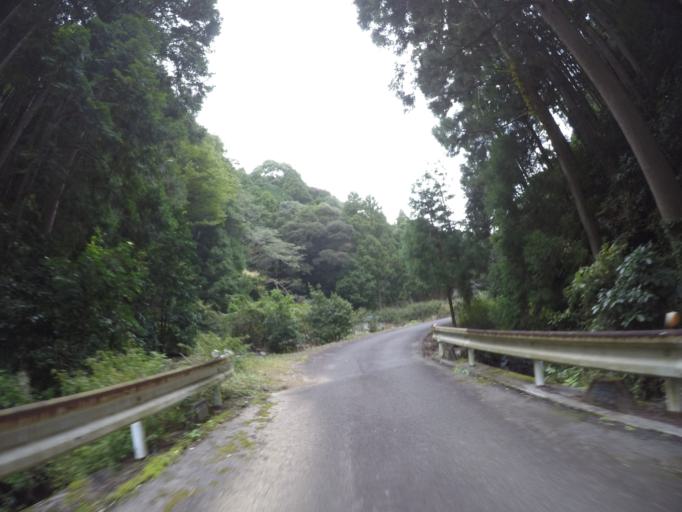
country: JP
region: Shizuoka
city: Shimada
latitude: 34.8890
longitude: 138.1678
